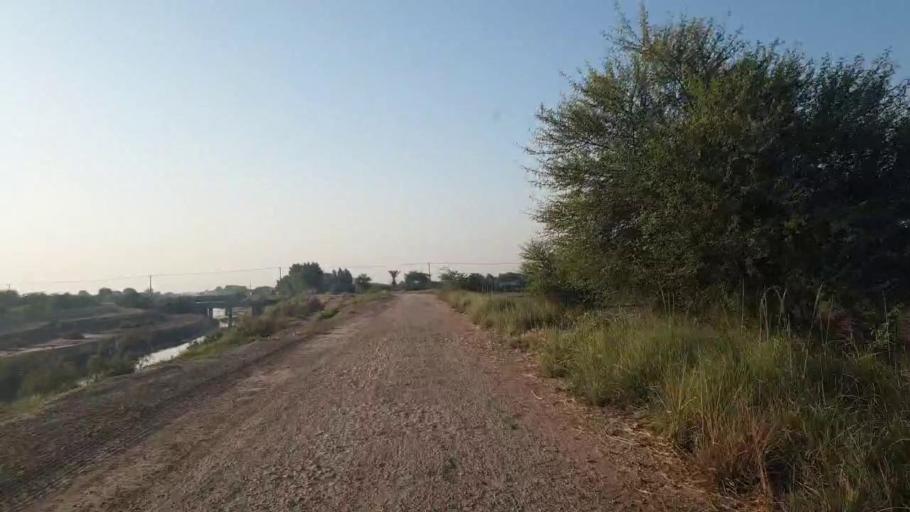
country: PK
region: Sindh
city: Badin
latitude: 24.6516
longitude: 68.7893
